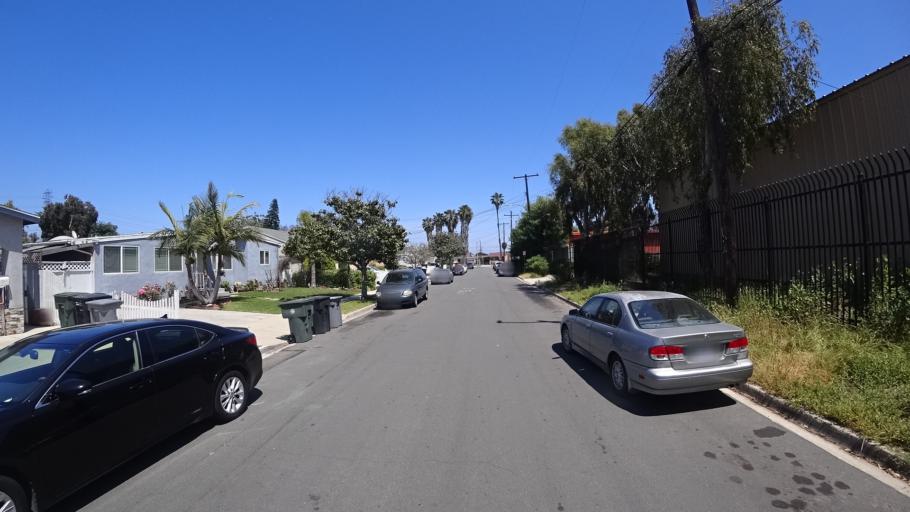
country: US
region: California
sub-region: Los Angeles County
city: Lawndale
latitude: 33.8675
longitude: -118.3480
